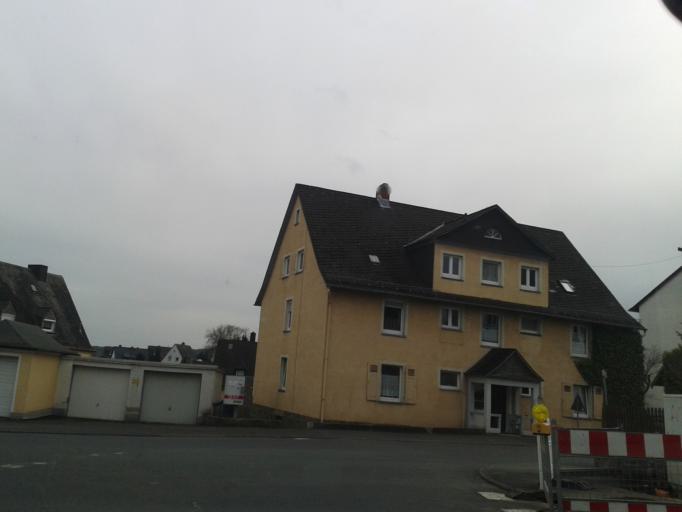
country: DE
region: Hesse
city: Herborn
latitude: 50.6814
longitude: 8.2981
